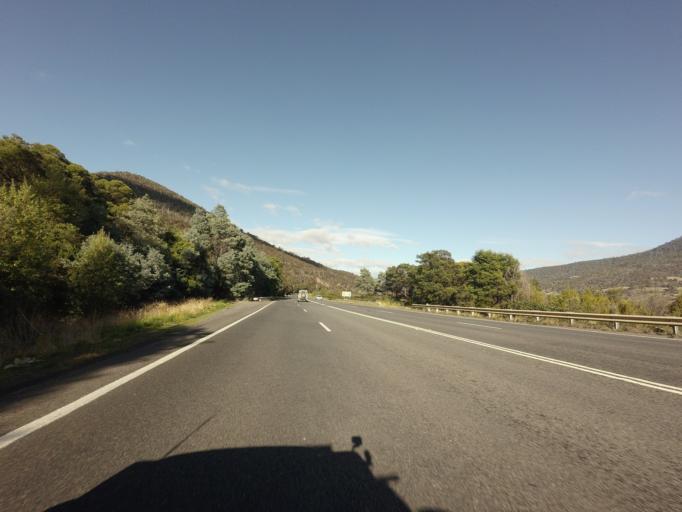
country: AU
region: Tasmania
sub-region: Glenorchy
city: Granton
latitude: -42.7543
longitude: 147.1626
